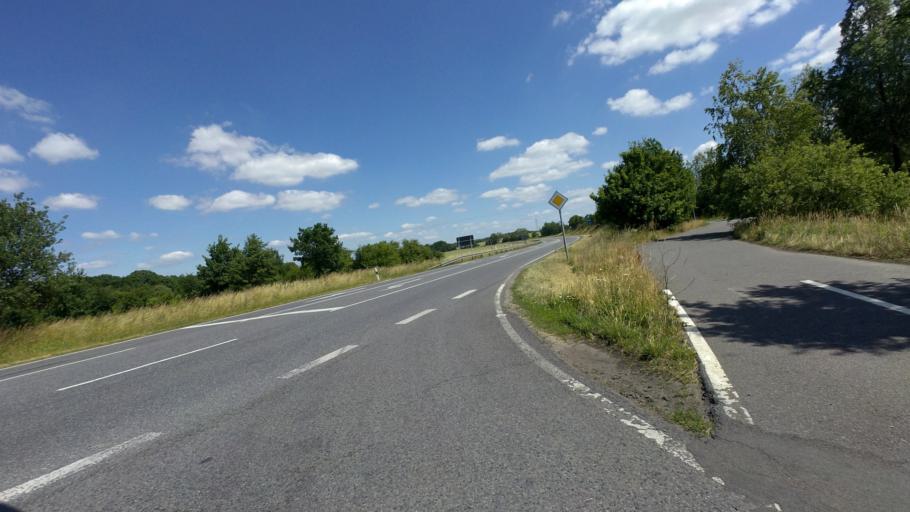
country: DE
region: Brandenburg
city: Luckau
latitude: 51.8428
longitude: 13.6774
